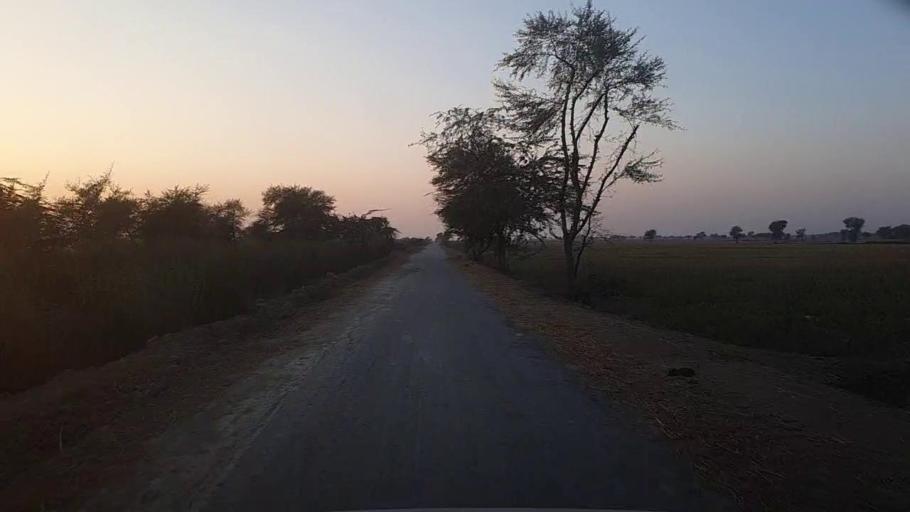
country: PK
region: Sindh
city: Khairpur Nathan Shah
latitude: 27.1584
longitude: 67.7131
